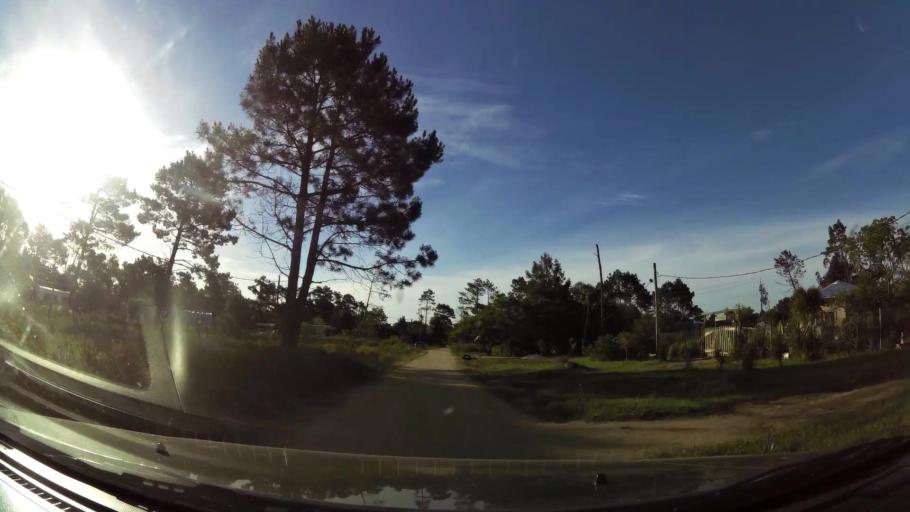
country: UY
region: Canelones
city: Empalme Olmos
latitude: -34.7689
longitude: -55.8599
